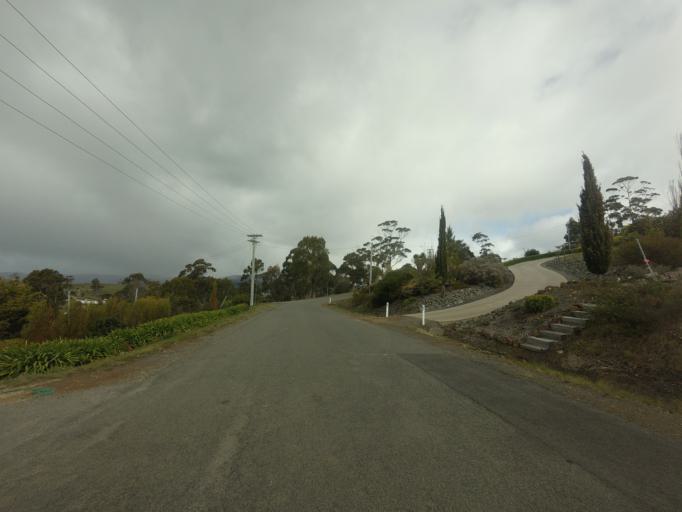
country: AU
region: Tasmania
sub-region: Sorell
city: Sorell
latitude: -42.5388
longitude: 147.9130
